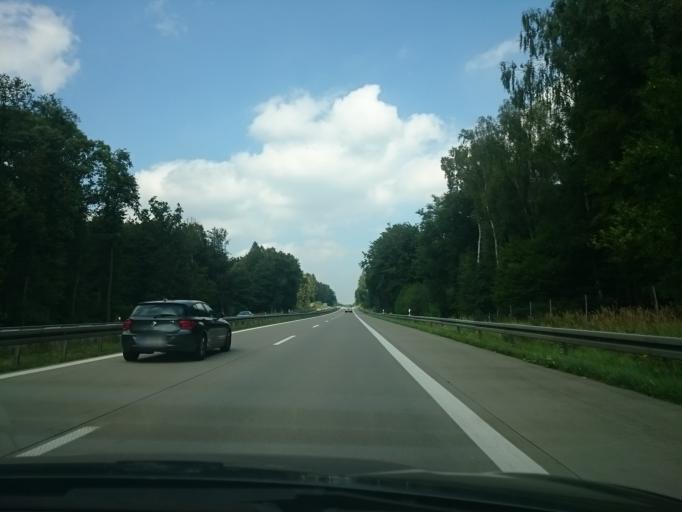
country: DE
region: Brandenburg
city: Althuttendorf
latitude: 53.0083
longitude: 13.8249
